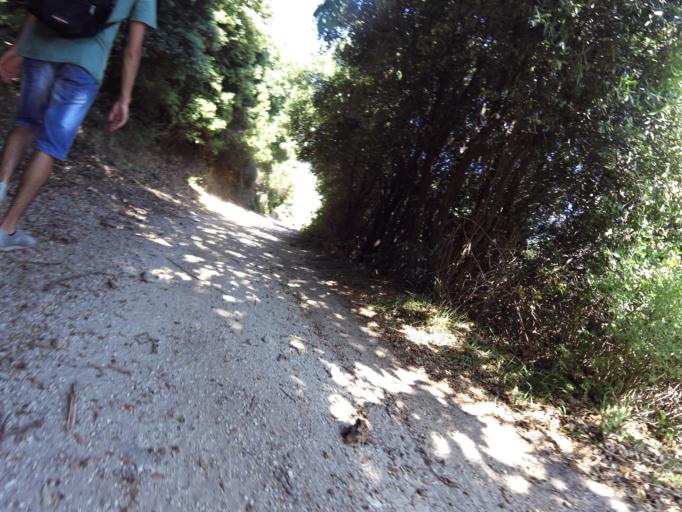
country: IT
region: Calabria
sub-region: Provincia di Reggio Calabria
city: Bivongi
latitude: 38.5032
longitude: 16.4412
